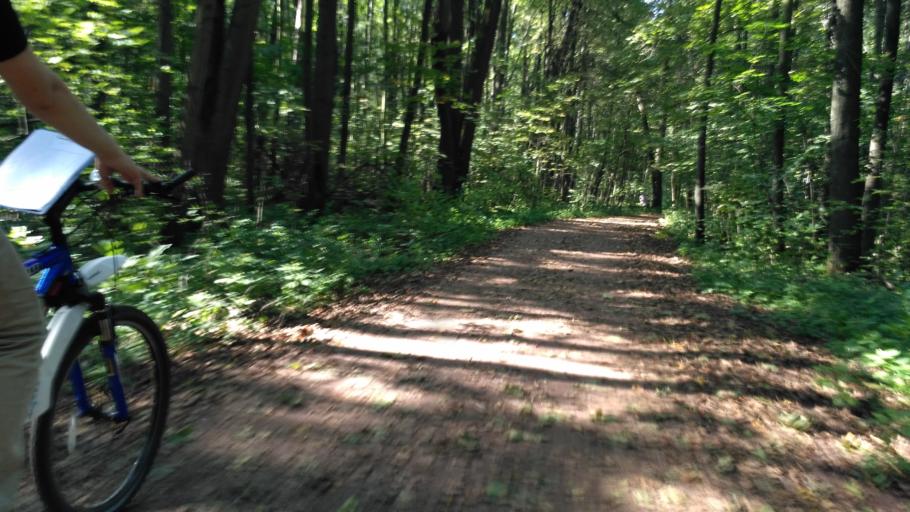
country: RU
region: Moskovskaya
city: Izmaylovo
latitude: 55.7833
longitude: 37.7730
